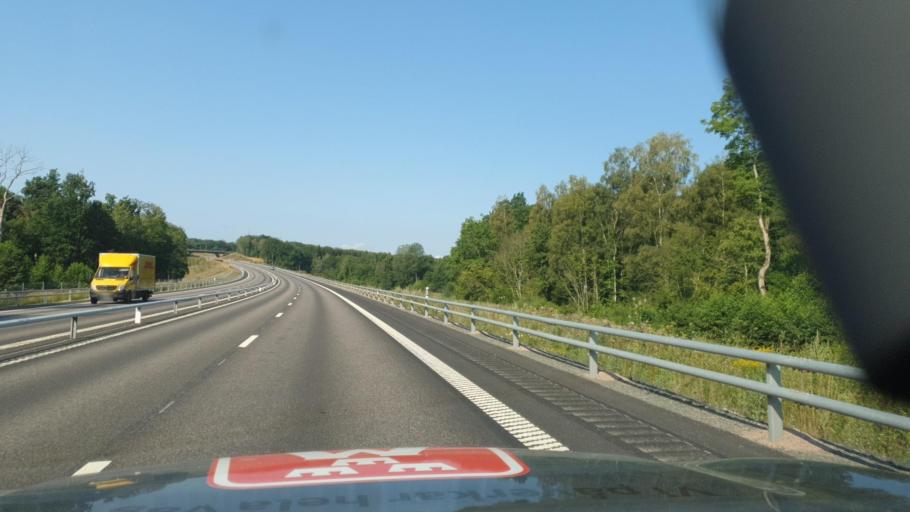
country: SE
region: Skane
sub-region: Hassleholms Kommun
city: Vinslov
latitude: 55.9505
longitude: 13.9035
